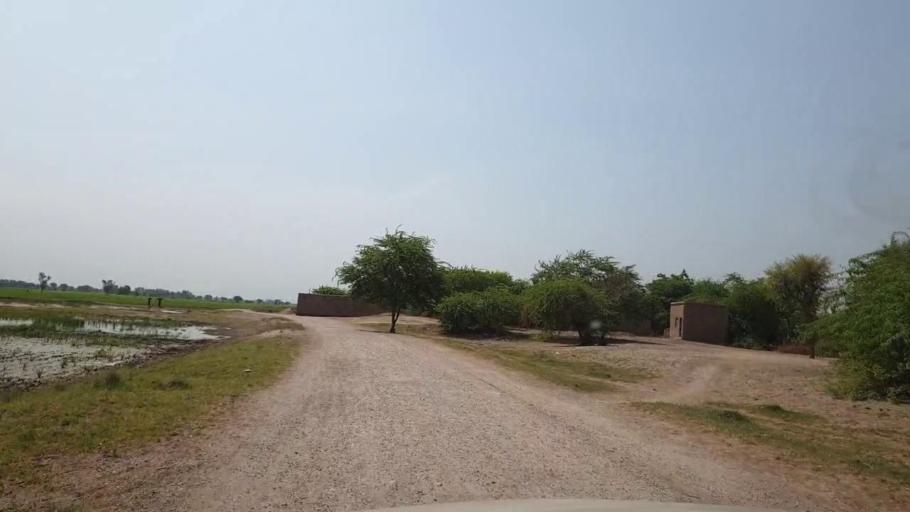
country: PK
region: Sindh
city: Ratodero
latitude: 27.8415
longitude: 68.2639
